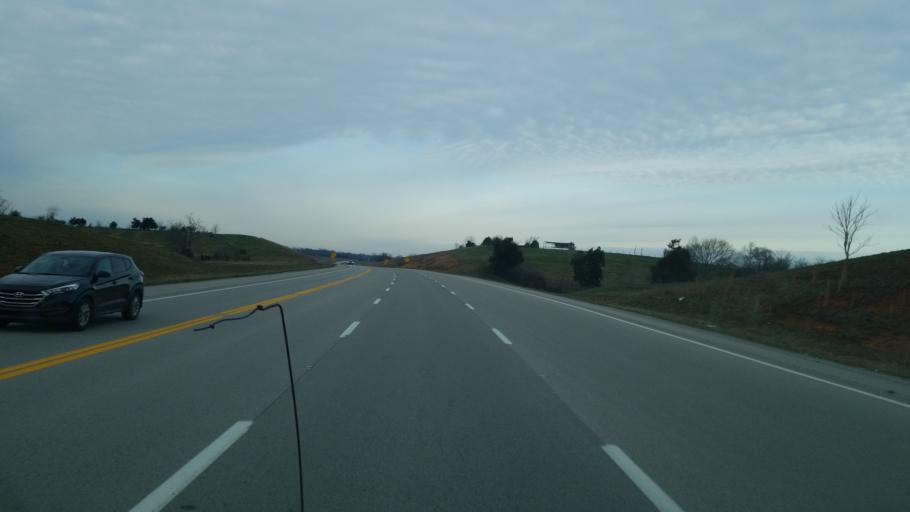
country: US
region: Kentucky
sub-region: Clinton County
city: Albany
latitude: 36.6634
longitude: -85.1192
